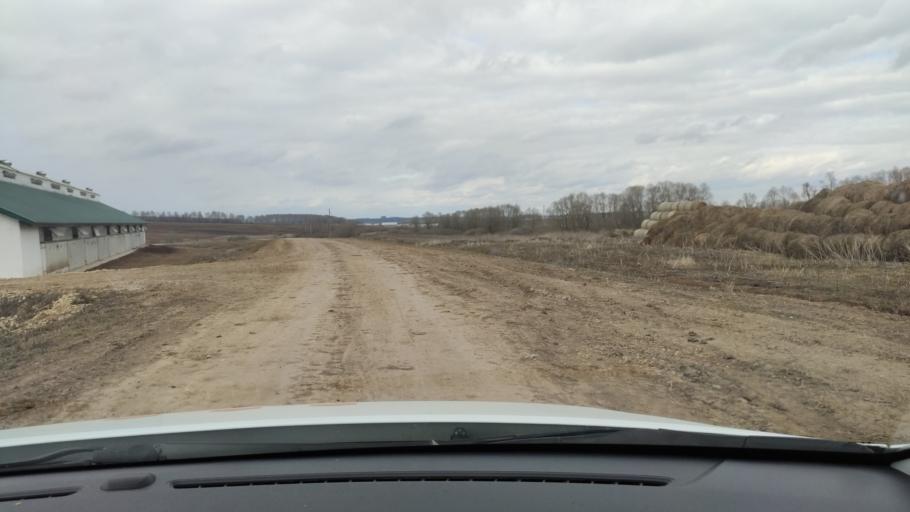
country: RU
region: Tatarstan
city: Vysokaya Gora
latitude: 56.2174
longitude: 49.3132
